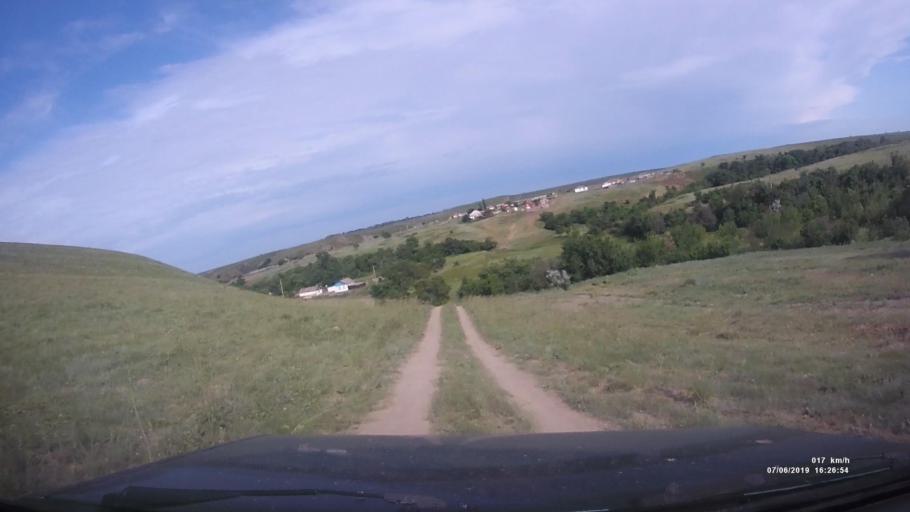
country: RU
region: Rostov
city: Kamensk-Shakhtinskiy
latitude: 48.2524
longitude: 40.3152
